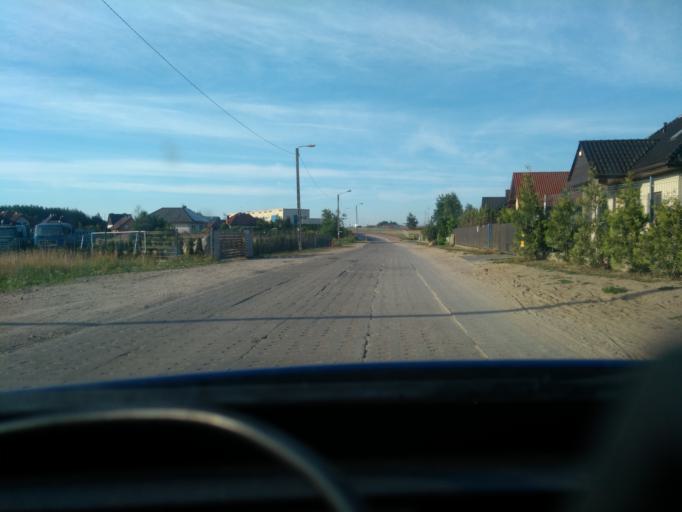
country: PL
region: Pomeranian Voivodeship
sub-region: Powiat kartuski
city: Banino
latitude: 54.3992
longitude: 18.3981
